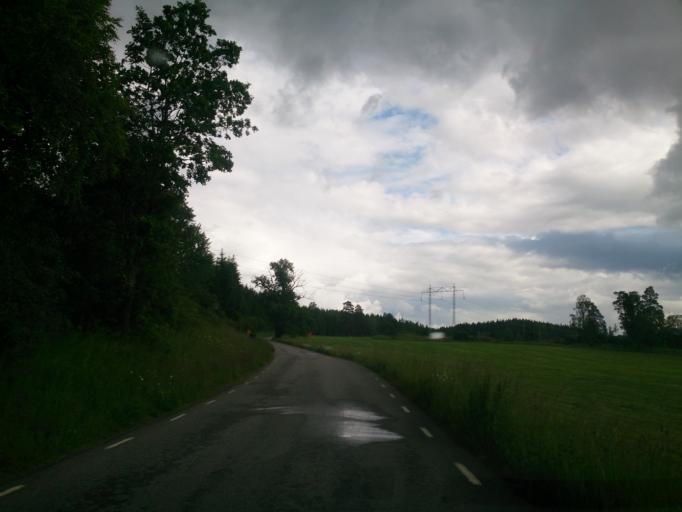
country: SE
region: OEstergoetland
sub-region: Atvidabergs Kommun
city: Atvidaberg
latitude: 58.3339
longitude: 16.0329
